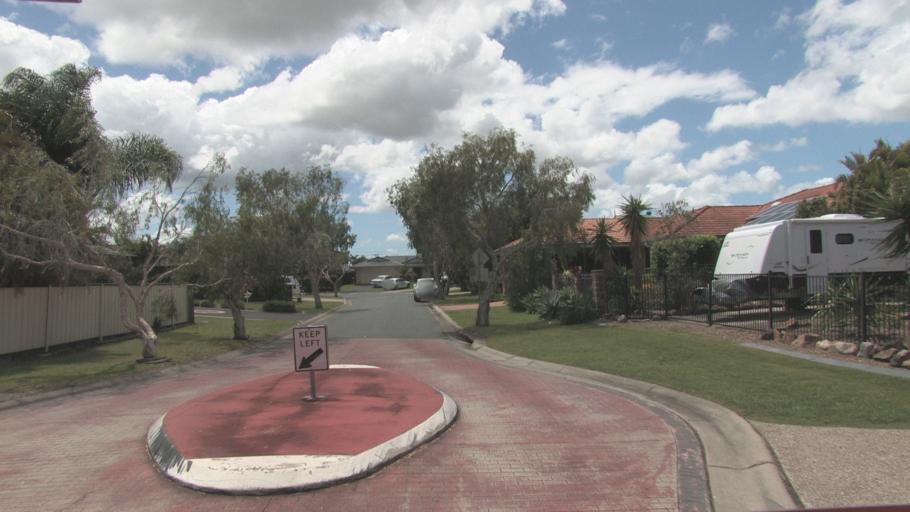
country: AU
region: Queensland
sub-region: Logan
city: Beenleigh
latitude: -27.6876
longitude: 153.1767
